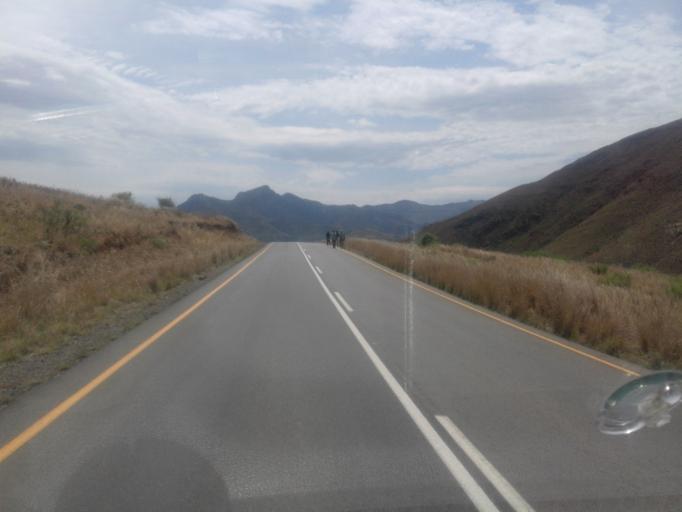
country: LS
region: Qacha's Nek
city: Qacha's Nek
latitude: -30.0845
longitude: 28.6331
